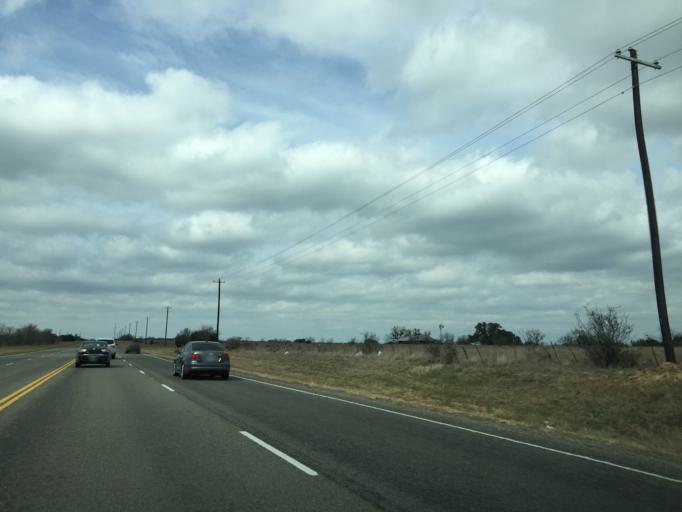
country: US
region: Texas
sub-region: Travis County
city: Briarcliff
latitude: 30.4695
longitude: -98.1748
